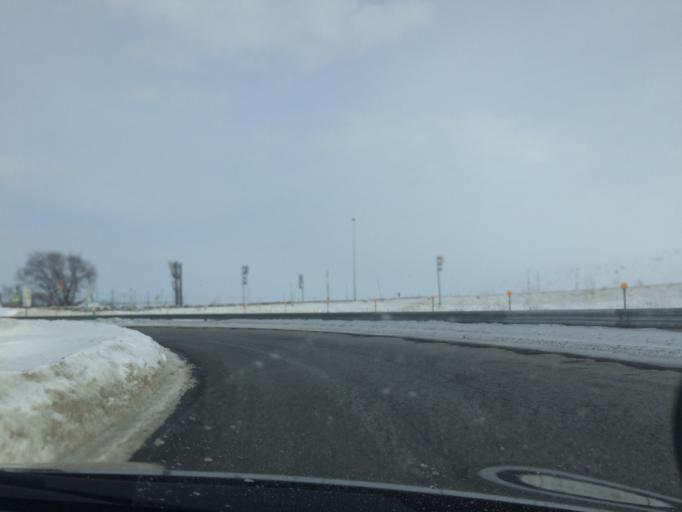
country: JP
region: Hokkaido
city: Otofuke
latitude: 42.9952
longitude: 142.8563
